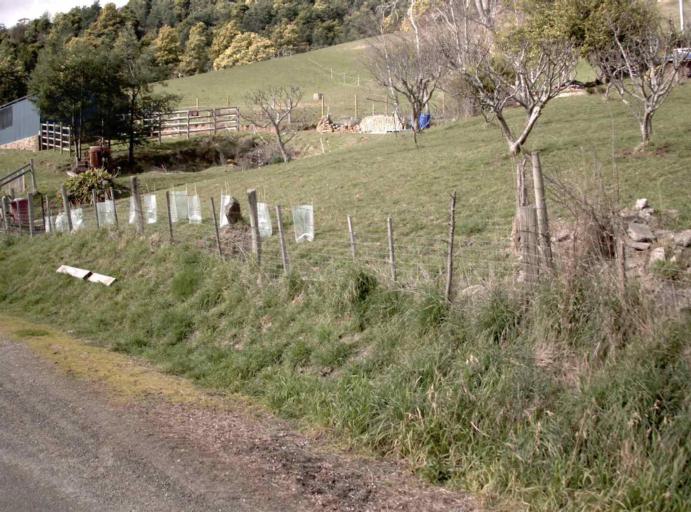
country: AU
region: Tasmania
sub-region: Launceston
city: Mayfield
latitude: -41.2527
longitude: 147.2446
